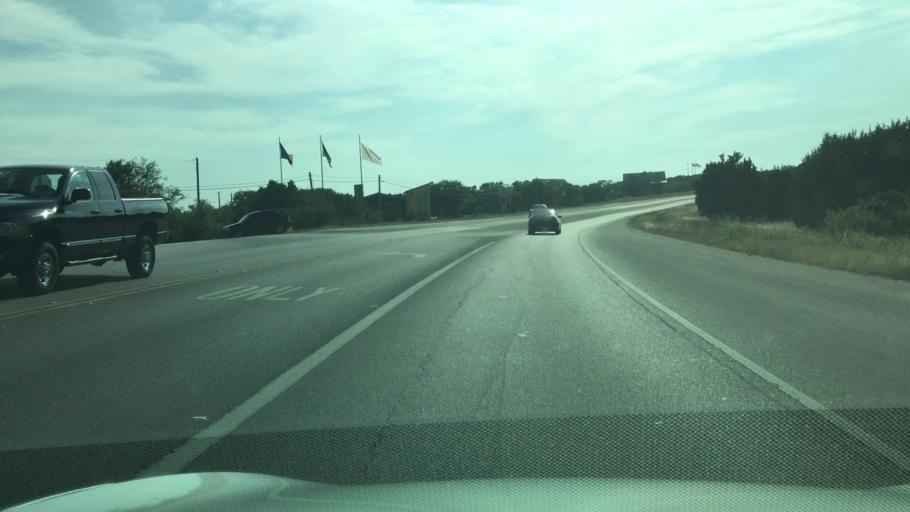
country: US
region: Texas
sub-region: Hays County
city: Wimberley
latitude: 29.9165
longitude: -98.0481
